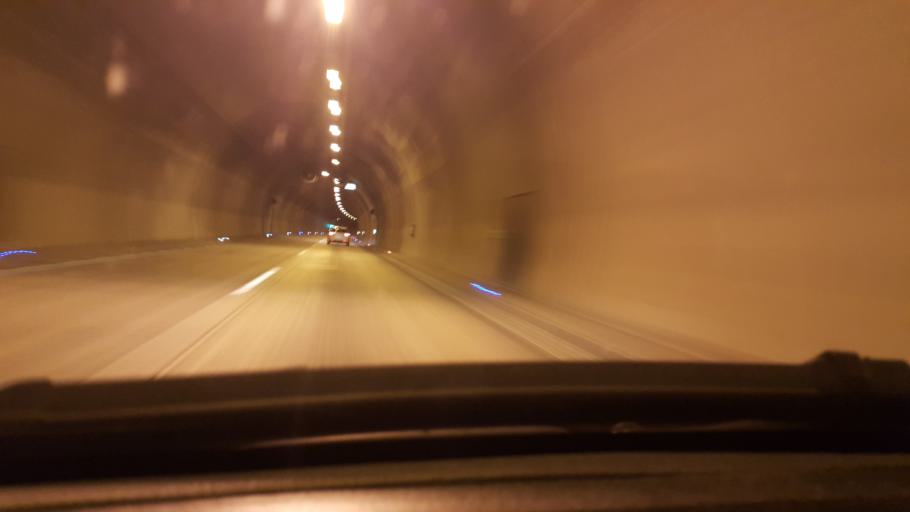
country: SI
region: Zagorje ob Savi
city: Izlake
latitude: 46.1842
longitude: 14.8629
